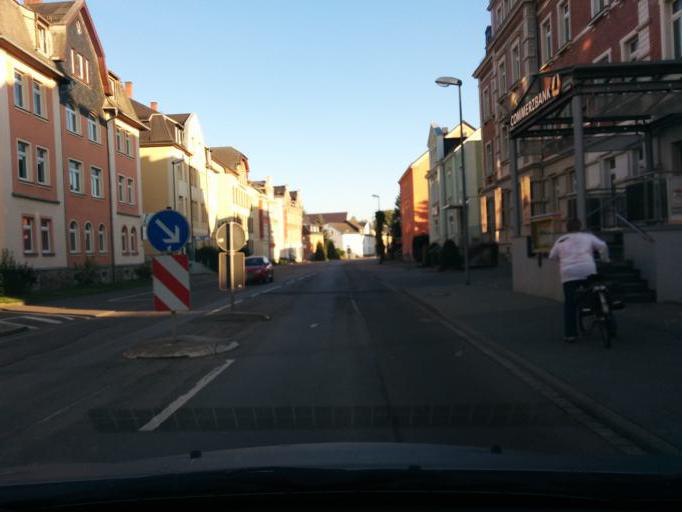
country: DE
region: Saxony
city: Floha
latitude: 50.8568
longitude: 13.0703
